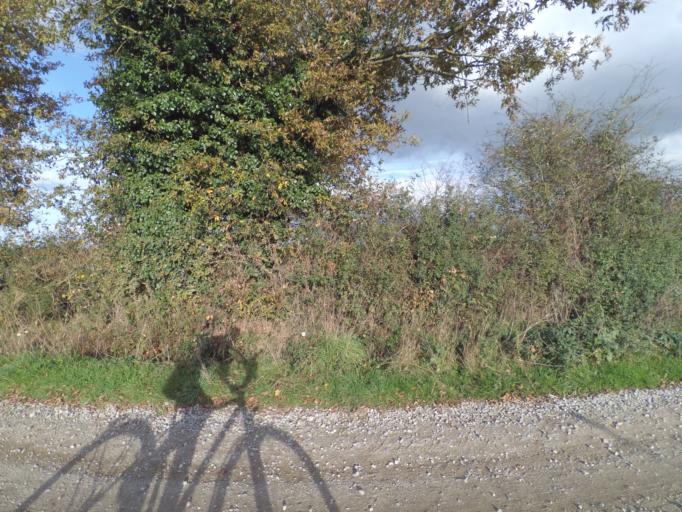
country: FR
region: Pays de la Loire
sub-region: Departement de la Vendee
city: Saint-Hilaire-de-Loulay
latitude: 47.0106
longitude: -1.3461
